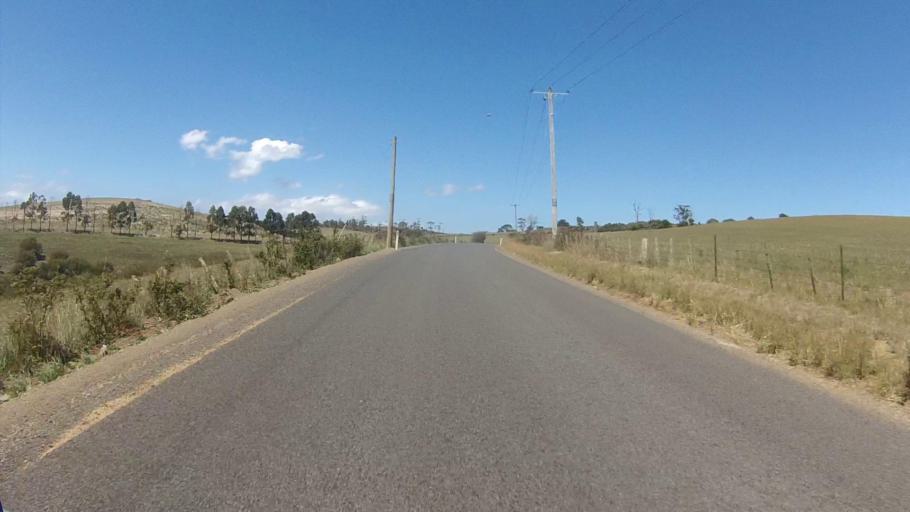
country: AU
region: Tasmania
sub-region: Sorell
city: Sorell
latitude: -42.7587
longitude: 147.6257
